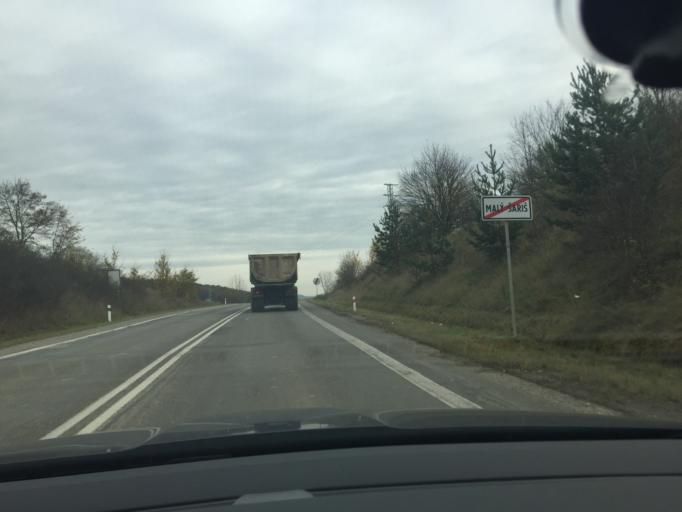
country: SK
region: Presovsky
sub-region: Okres Presov
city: Presov
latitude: 49.0038
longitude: 21.1833
